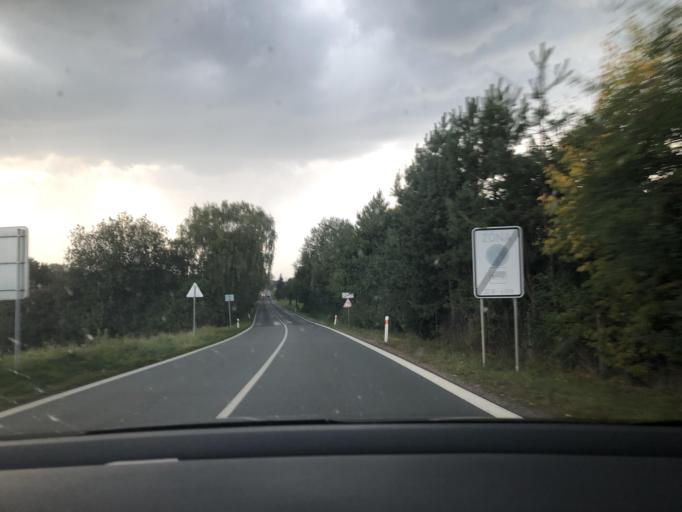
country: CZ
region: Central Bohemia
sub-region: Okres Kolin
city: Tynec nad Labem
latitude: 50.0374
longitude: 15.3372
